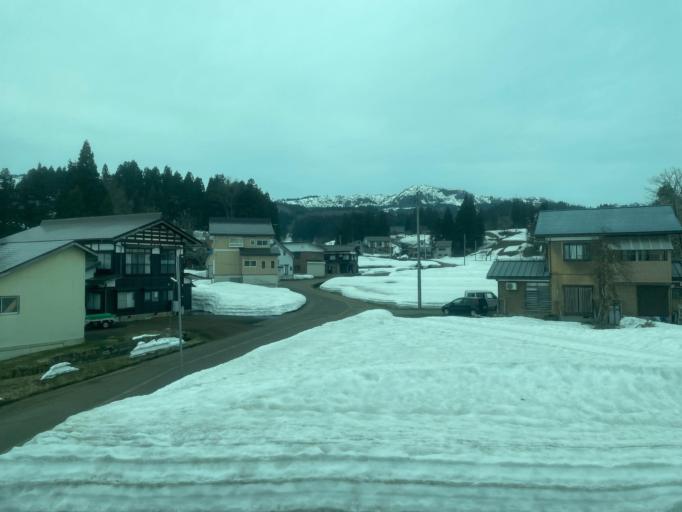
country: JP
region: Niigata
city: Shiozawa
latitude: 37.0351
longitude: 138.8373
